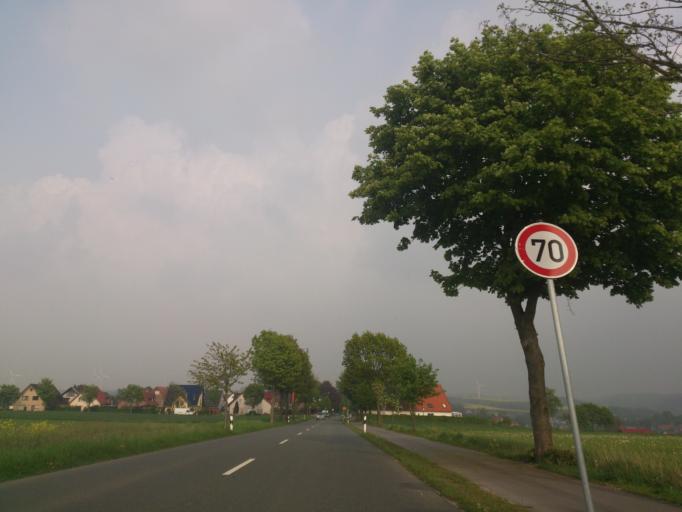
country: DE
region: North Rhine-Westphalia
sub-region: Regierungsbezirk Detmold
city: Paderborn
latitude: 51.6988
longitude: 8.8341
